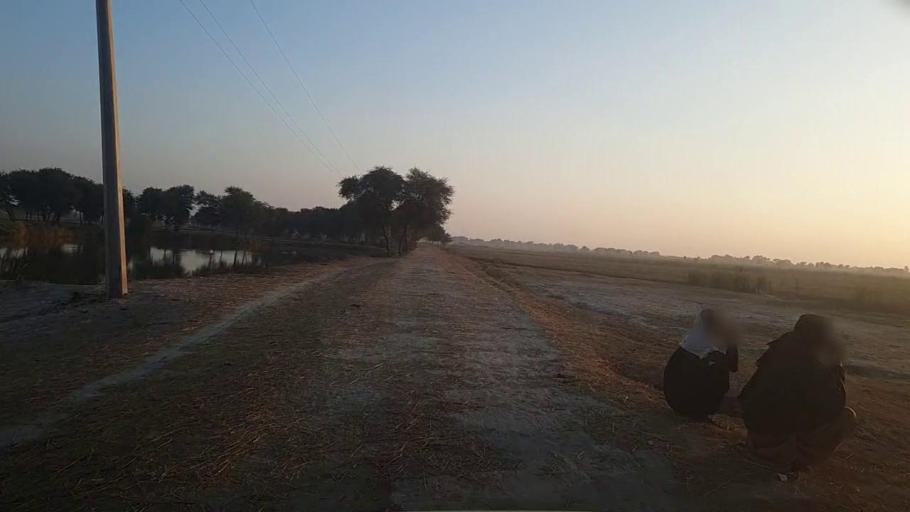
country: PK
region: Sindh
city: Khairpur Nathan Shah
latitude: 27.1690
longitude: 67.7325
